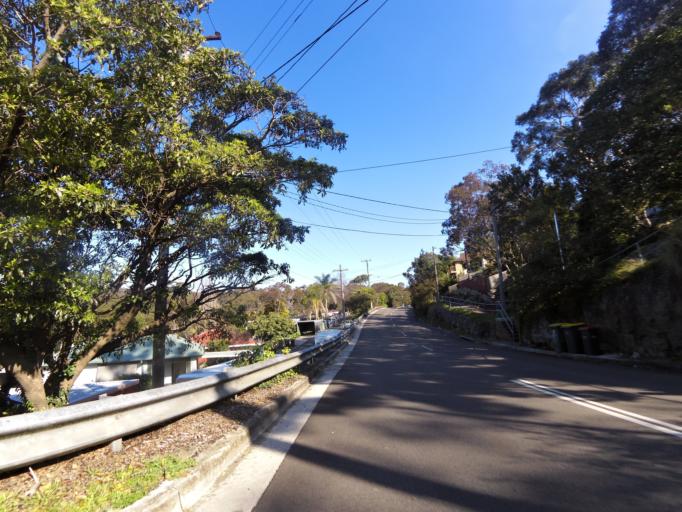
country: AU
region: New South Wales
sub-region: Sutherland Shire
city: Oyster Bay
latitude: -34.0076
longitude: 151.0696
